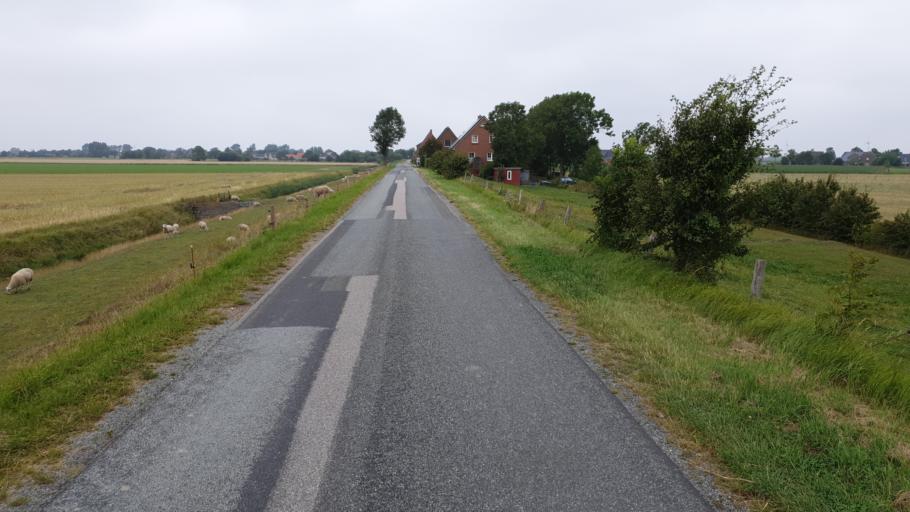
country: DE
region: Schleswig-Holstein
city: Elisabeth-Sophien-Koog
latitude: 54.4838
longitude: 8.8906
